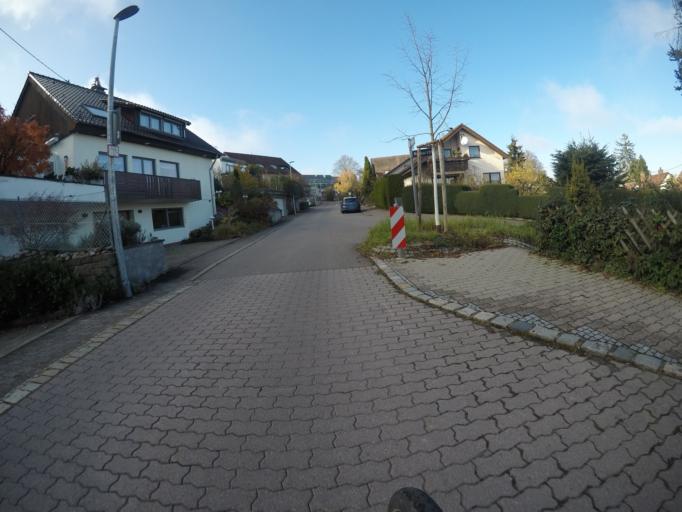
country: DE
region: Baden-Wuerttemberg
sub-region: Regierungsbezirk Stuttgart
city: Steinenbronn
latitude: 48.7144
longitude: 9.1065
